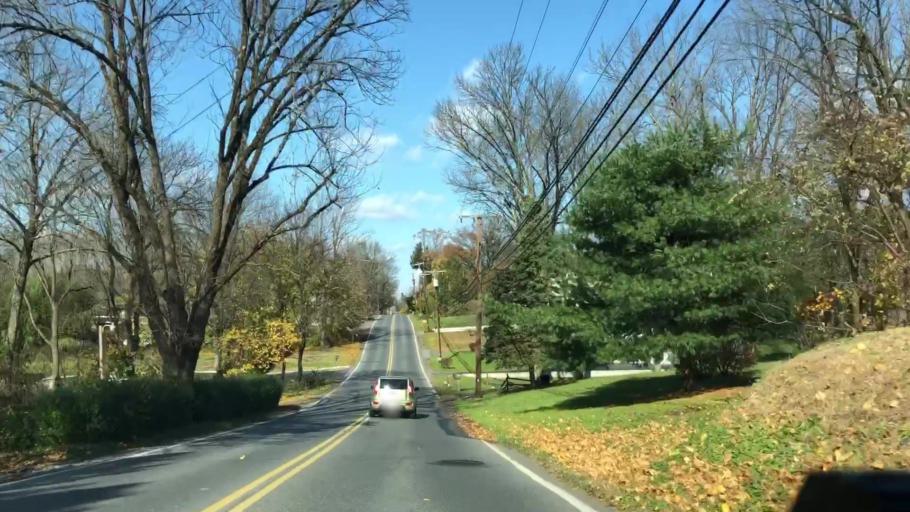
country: US
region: Pennsylvania
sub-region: Montgomery County
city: Halfway House
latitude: 40.2691
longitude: -75.6414
